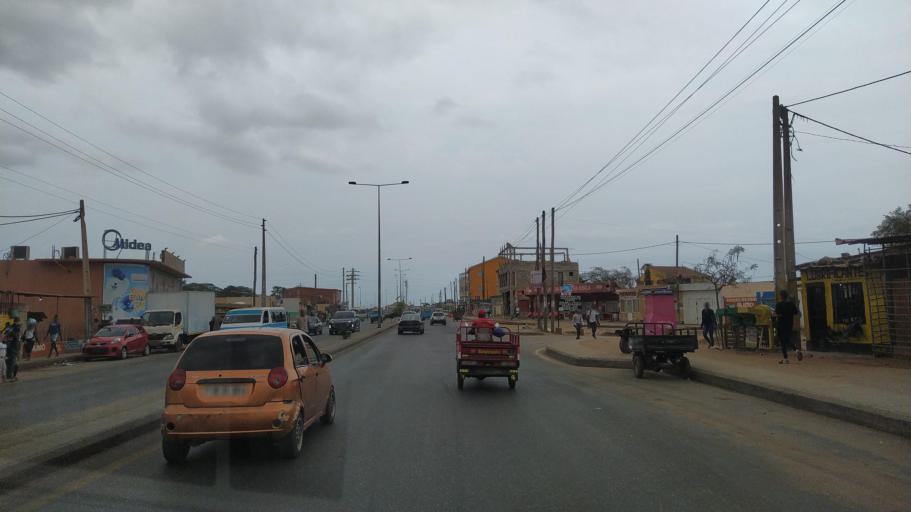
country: AO
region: Luanda
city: Luanda
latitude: -8.8757
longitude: 13.2728
